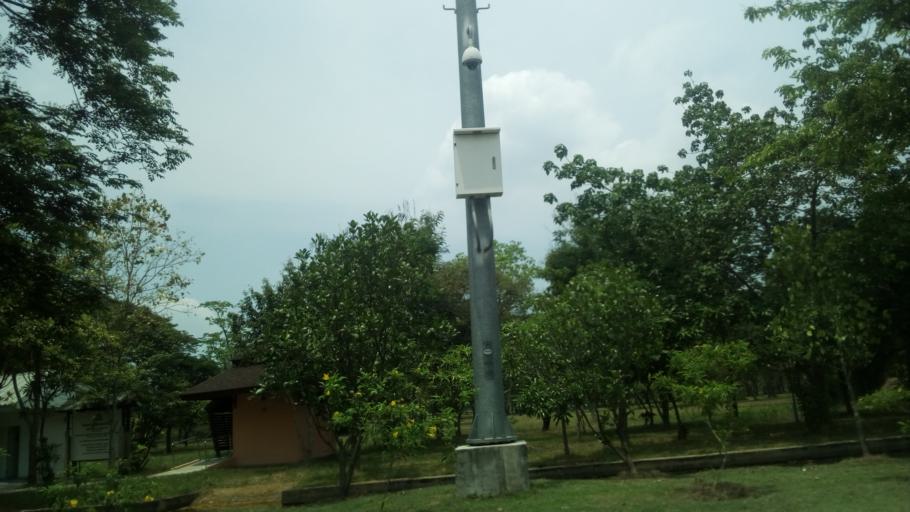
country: TH
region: Bangkok
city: Thawi Watthana
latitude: 13.7725
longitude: 100.3250
